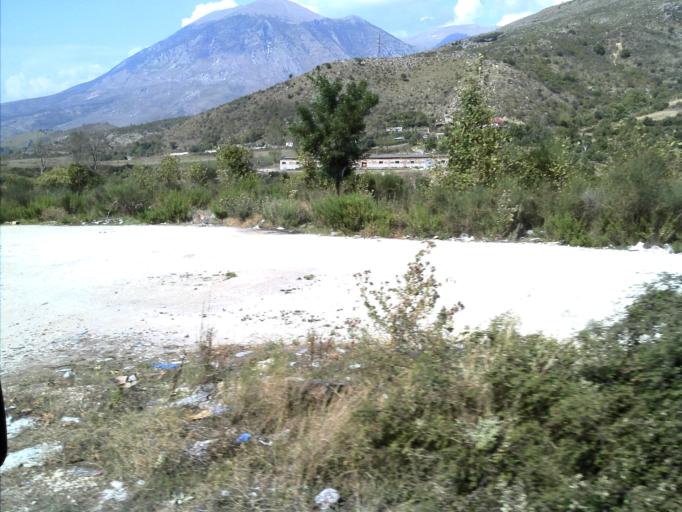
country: AL
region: Gjirokaster
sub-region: Rrethi i Tepelenes
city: Tepelene
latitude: 40.2556
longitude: 20.0588
